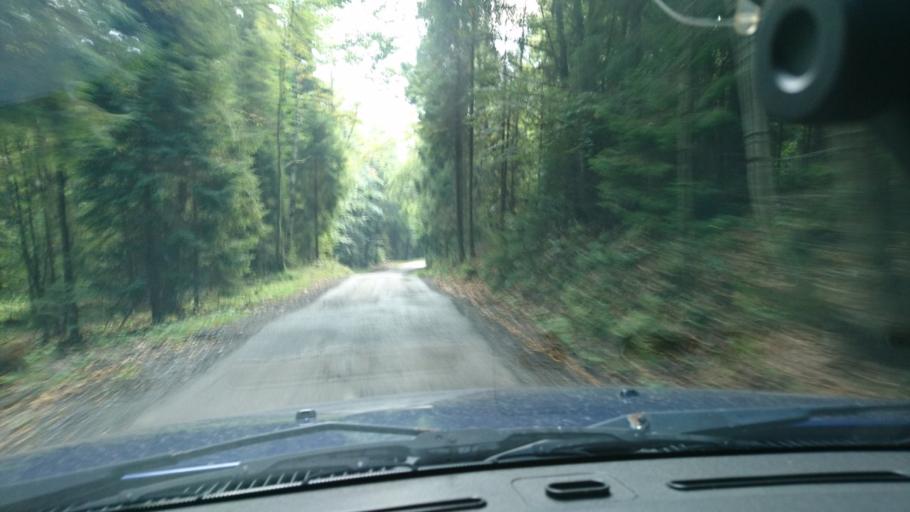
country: PL
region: Silesian Voivodeship
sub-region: Powiat bielski
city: Wilkowice
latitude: 49.7679
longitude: 19.1176
